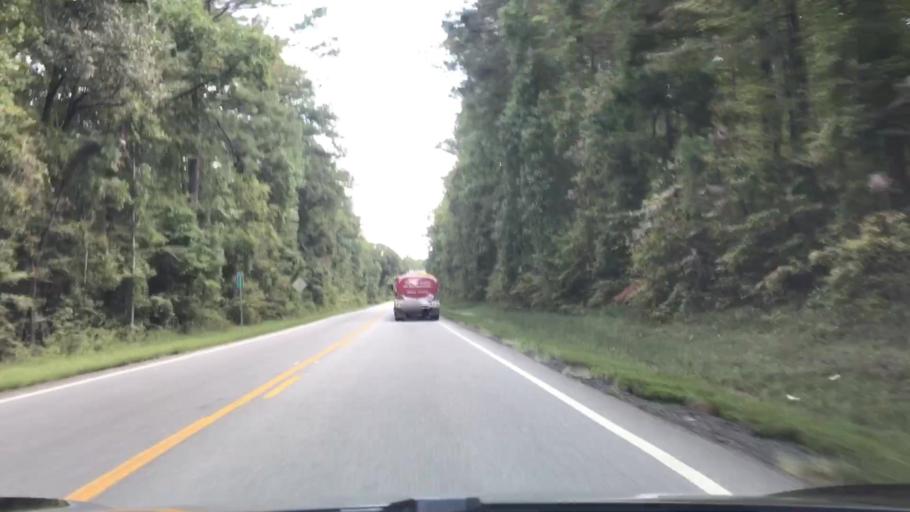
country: US
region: Georgia
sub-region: Greene County
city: Greensboro
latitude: 33.6994
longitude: -83.2811
